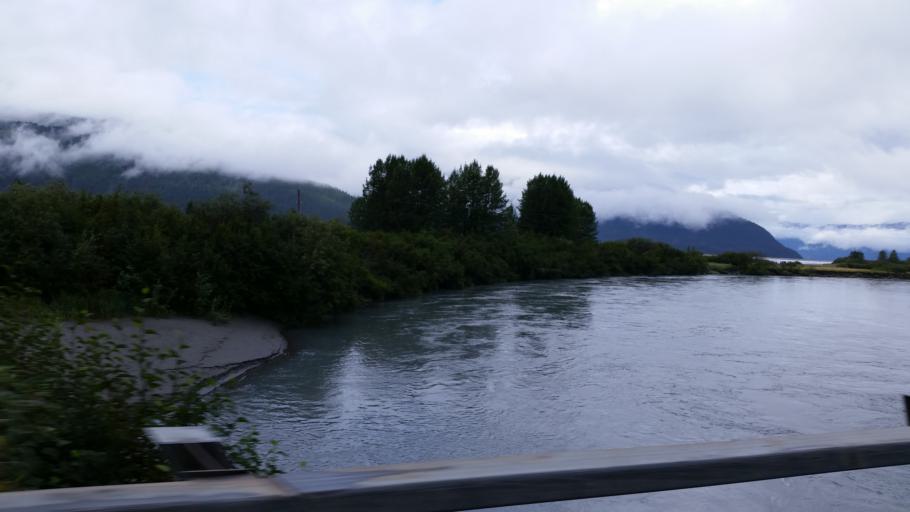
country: US
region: Alaska
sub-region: Anchorage Municipality
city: Girdwood
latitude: 60.8269
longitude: -148.9778
